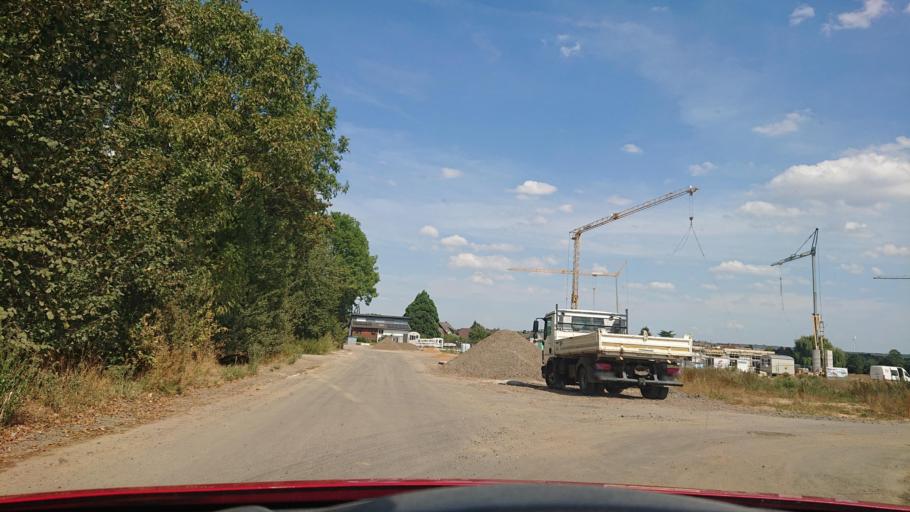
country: DE
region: North Rhine-Westphalia
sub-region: Regierungsbezirk Koln
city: Bergheim
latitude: 50.9347
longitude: 6.6365
